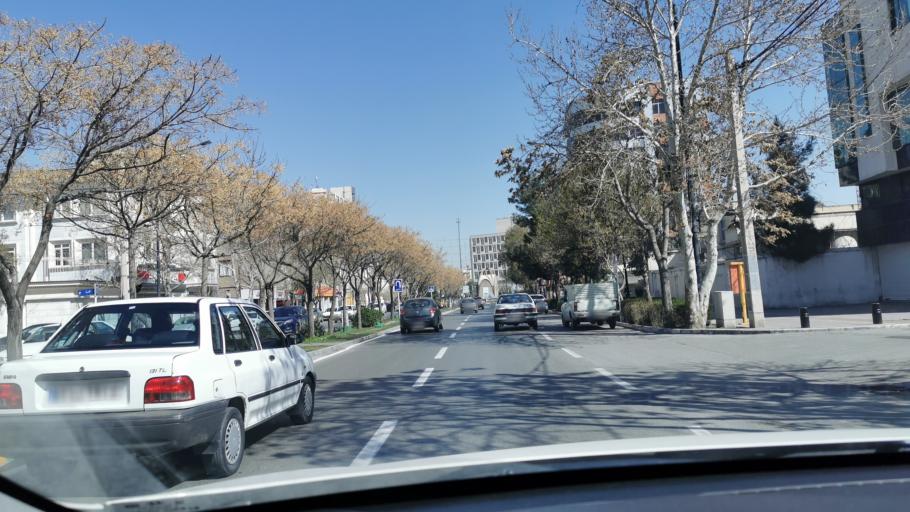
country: IR
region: Razavi Khorasan
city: Mashhad
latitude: 36.2951
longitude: 59.5728
